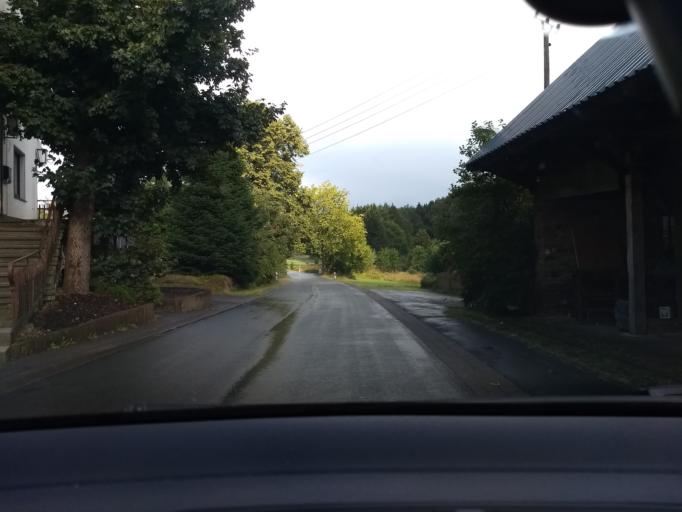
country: DE
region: North Rhine-Westphalia
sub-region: Regierungsbezirk Arnsberg
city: Finnentrop
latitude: 51.2222
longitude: 8.0377
